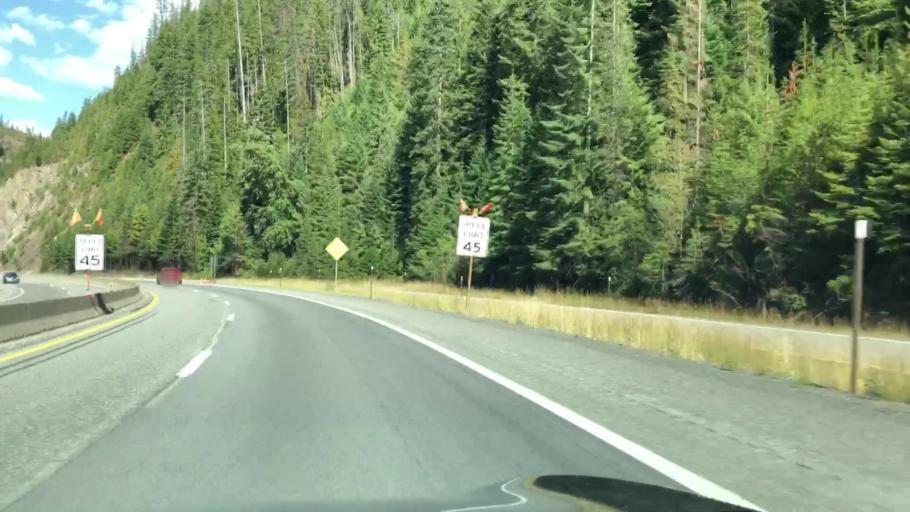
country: US
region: Idaho
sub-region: Shoshone County
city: Wallace
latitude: 47.4610
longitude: -115.8222
